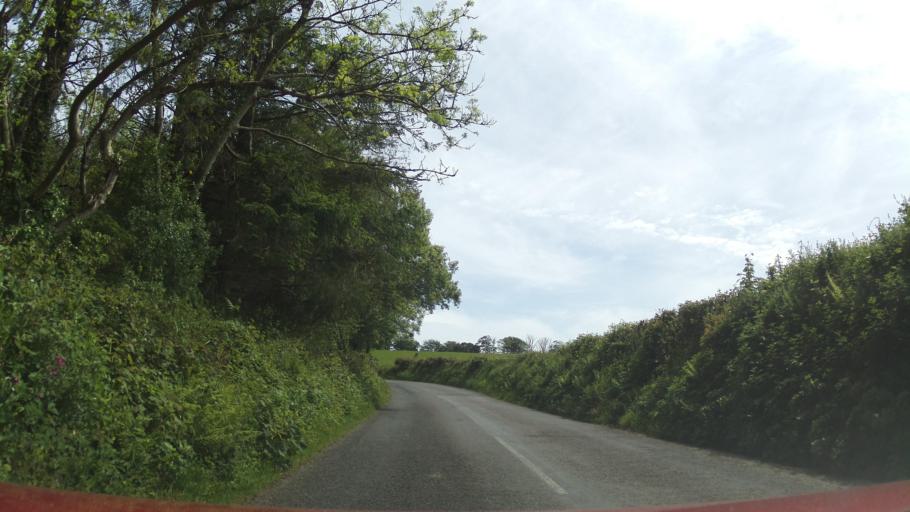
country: GB
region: England
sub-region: Devon
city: Kingsbridge
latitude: 50.3632
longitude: -3.7690
